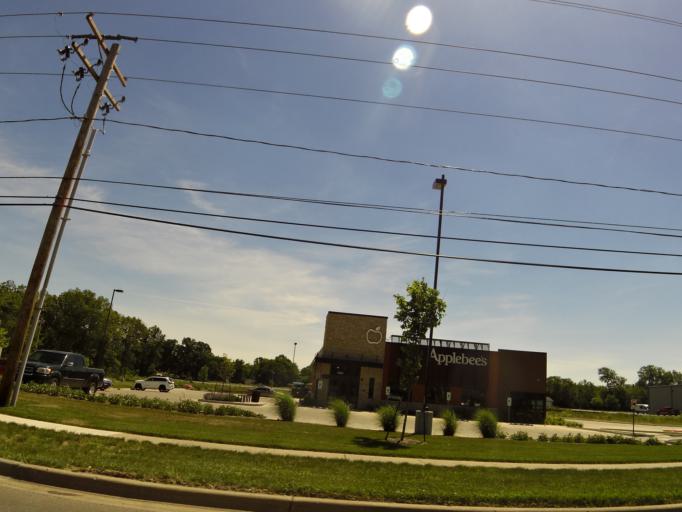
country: US
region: Illinois
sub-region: Vermilion County
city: Danville
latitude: 40.1809
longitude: -87.6298
